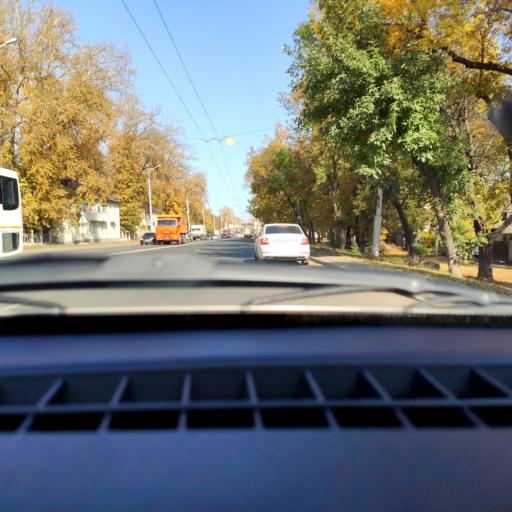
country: RU
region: Bashkortostan
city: Ufa
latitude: 54.8231
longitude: 56.1112
